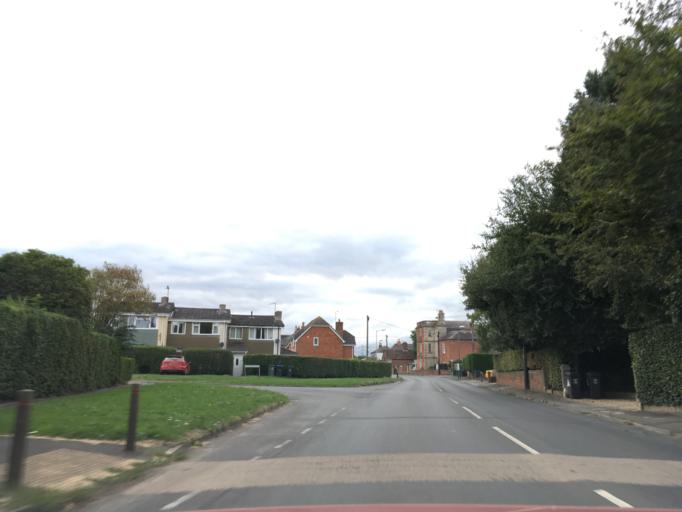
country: GB
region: England
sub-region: Wiltshire
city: Devizes
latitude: 51.3629
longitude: -2.0287
